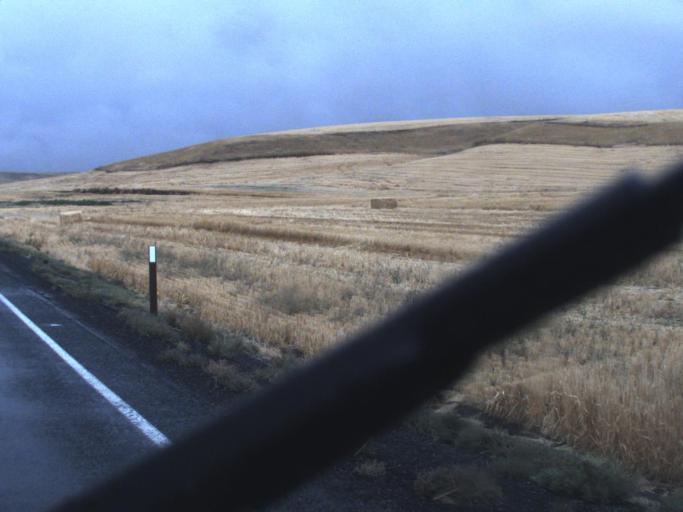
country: US
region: Washington
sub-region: Spokane County
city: Cheney
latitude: 47.1474
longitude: -117.8372
